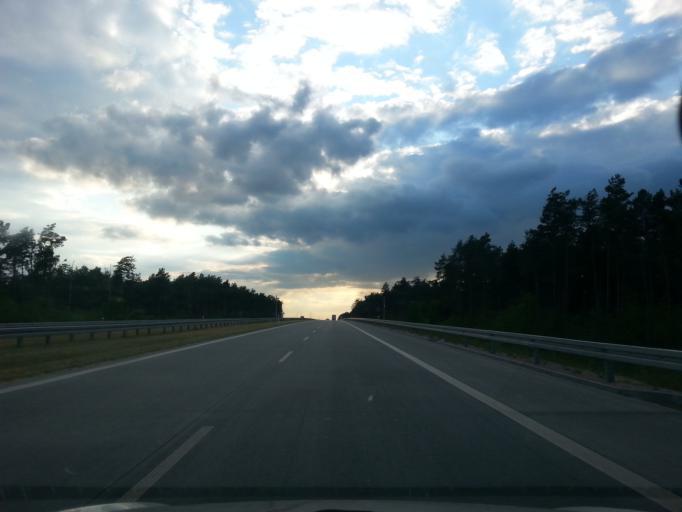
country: PL
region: Lodz Voivodeship
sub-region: Powiat zdunskowolski
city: Zdunska Wola
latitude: 51.5723
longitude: 18.9574
